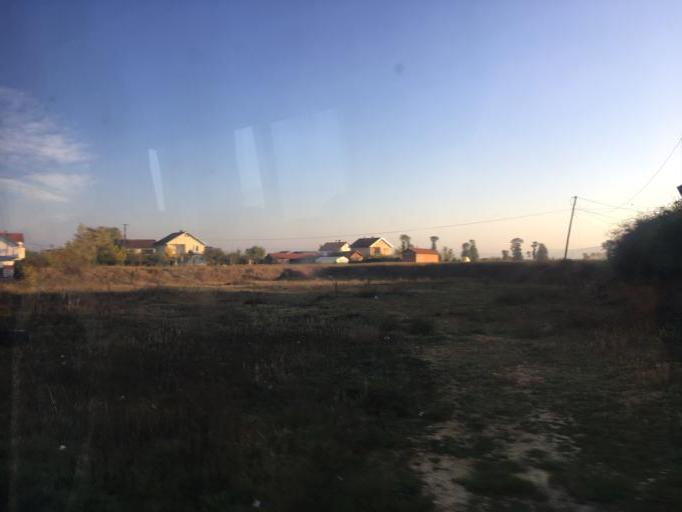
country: XK
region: Pristina
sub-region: Komuna e Drenasit
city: Glogovac
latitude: 42.5918
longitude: 20.8920
